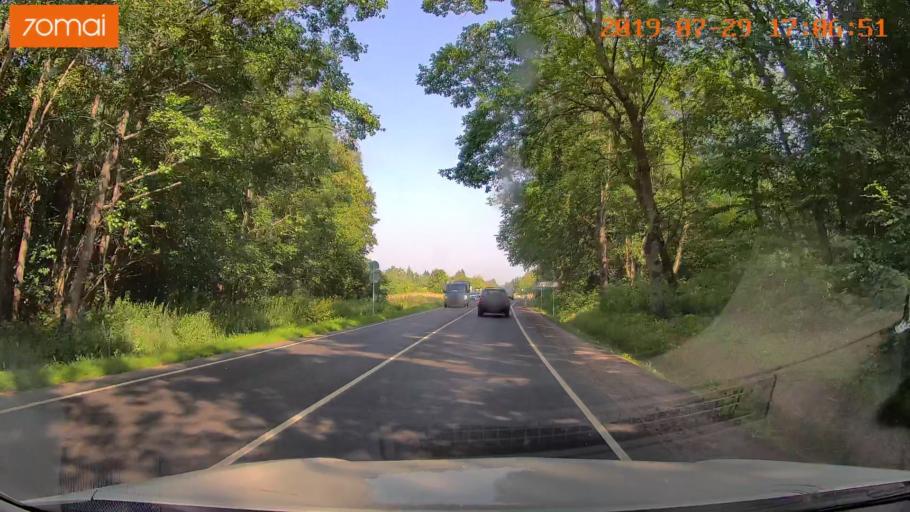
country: RU
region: Kaliningrad
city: Vzmorye
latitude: 54.8190
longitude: 20.3137
